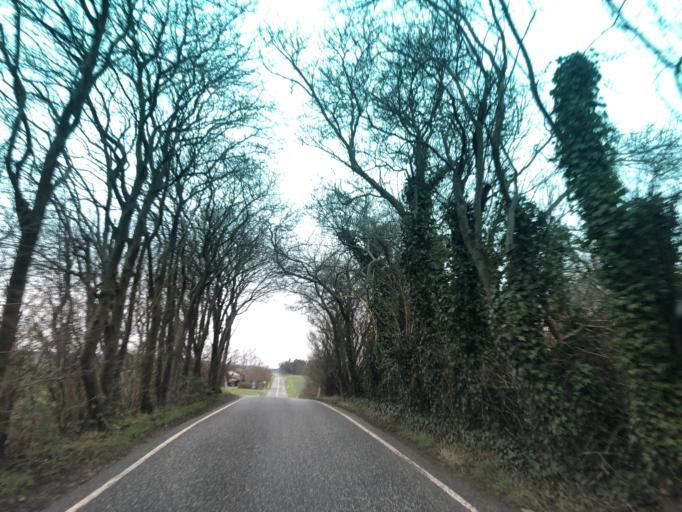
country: DK
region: Capital Region
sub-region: Allerod Kommune
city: Lynge
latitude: 55.8481
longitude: 12.2483
